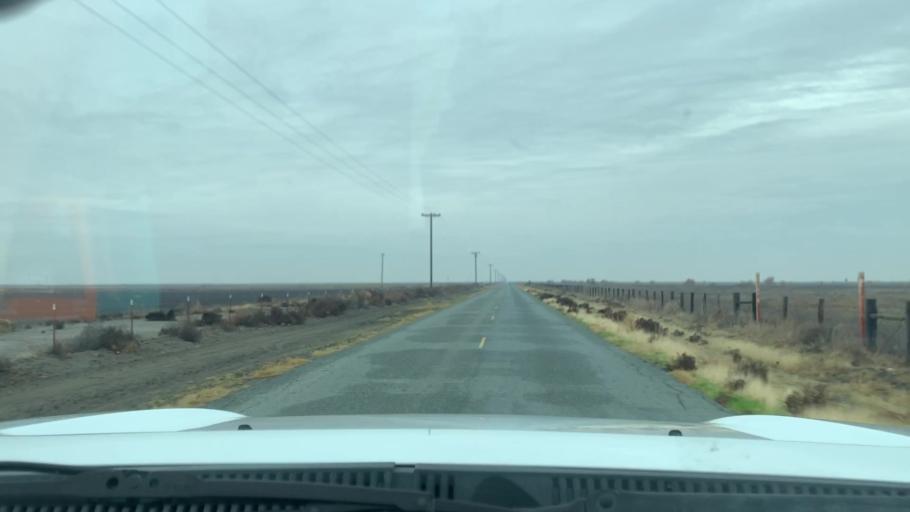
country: US
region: California
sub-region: Tulare County
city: Alpaugh
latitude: 35.7608
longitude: -119.5462
